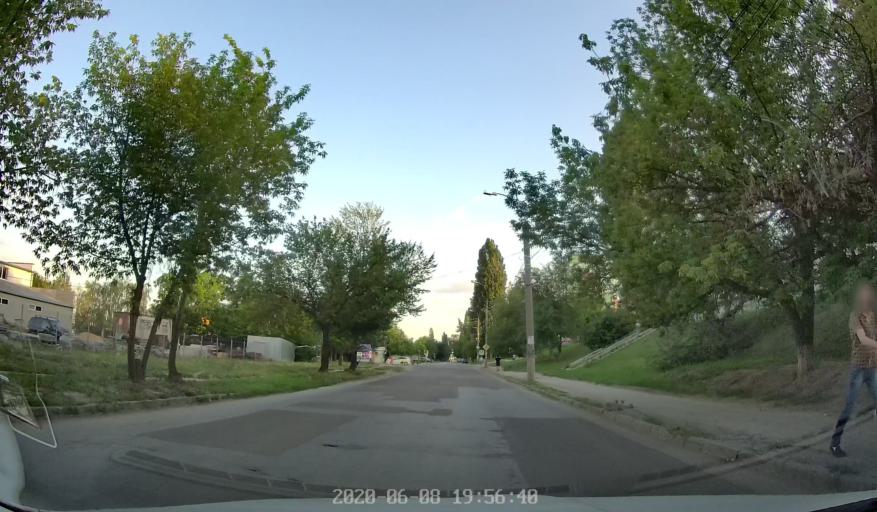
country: MD
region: Chisinau
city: Chisinau
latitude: 47.0207
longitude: 28.8830
